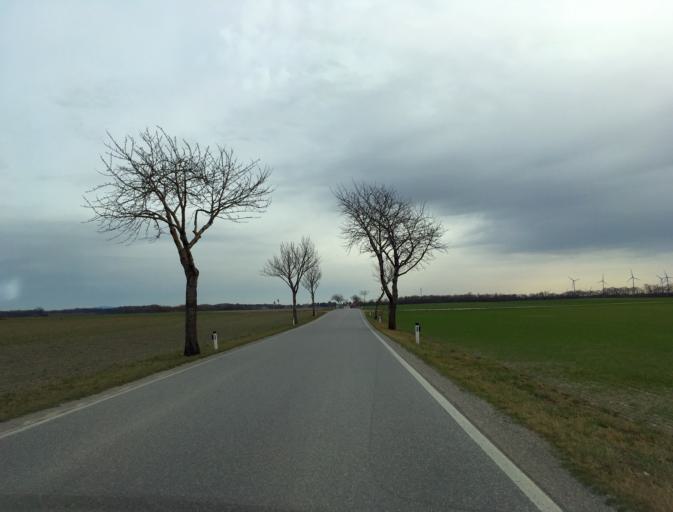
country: AT
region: Lower Austria
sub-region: Politischer Bezirk Ganserndorf
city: Leopoldsdorf im Marchfelde
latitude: 48.2395
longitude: 16.6696
